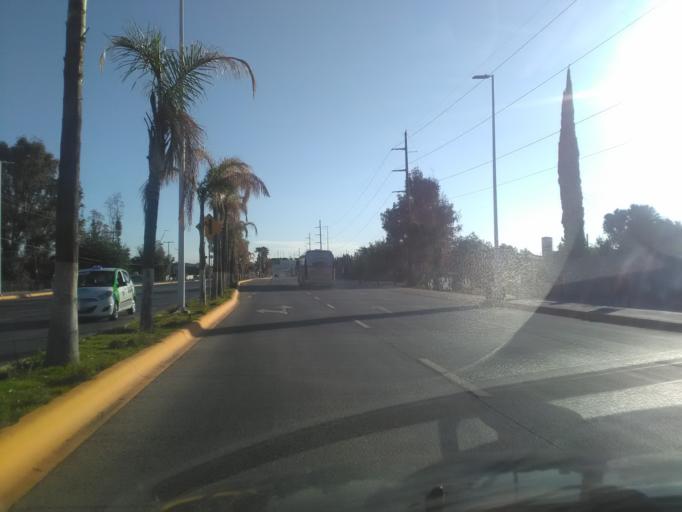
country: MX
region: Durango
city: Victoria de Durango
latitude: 23.9956
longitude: -104.7033
